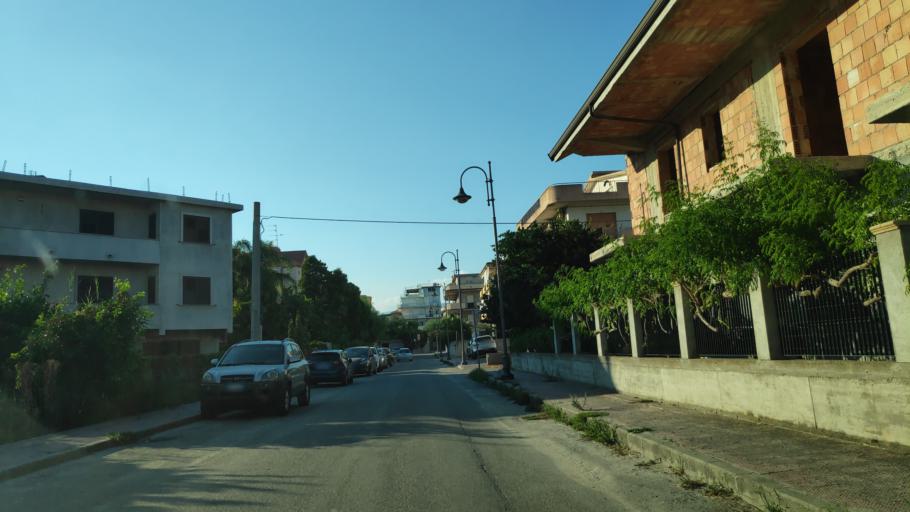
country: IT
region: Calabria
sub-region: Provincia di Reggio Calabria
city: Caulonia Marina
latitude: 38.3434
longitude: 16.4695
